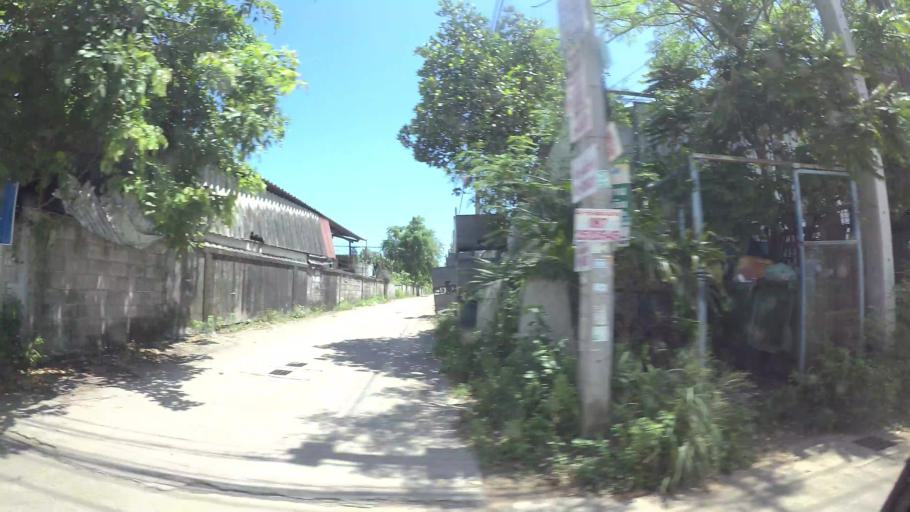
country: TH
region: Chon Buri
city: Si Racha
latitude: 13.1316
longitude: 100.9538
